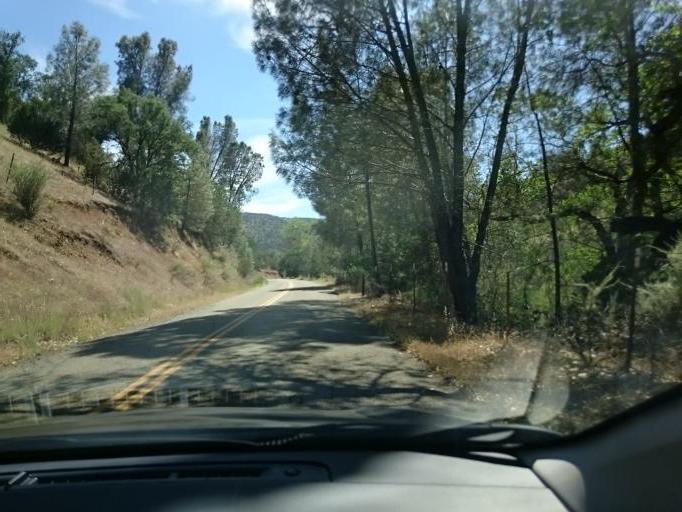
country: US
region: California
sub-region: Stanislaus County
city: Patterson
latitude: 37.4278
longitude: -121.3396
